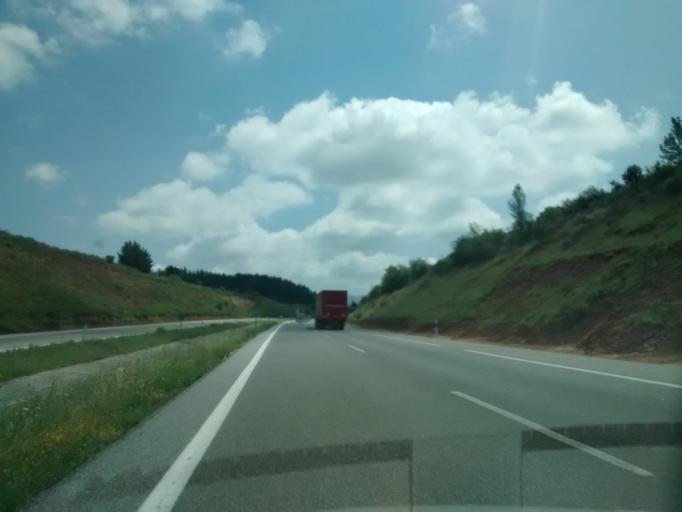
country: ES
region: Castille and Leon
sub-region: Provincia de Leon
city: Ponferrada
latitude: 42.5681
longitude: -6.5874
